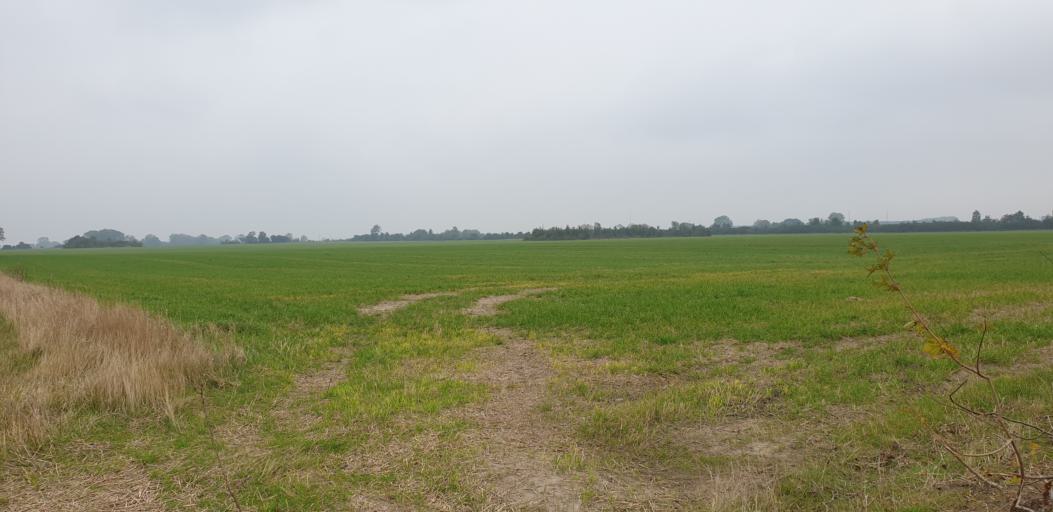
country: DK
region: Zealand
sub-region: Stevns Kommune
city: Harlev
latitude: 55.3347
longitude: 12.1956
